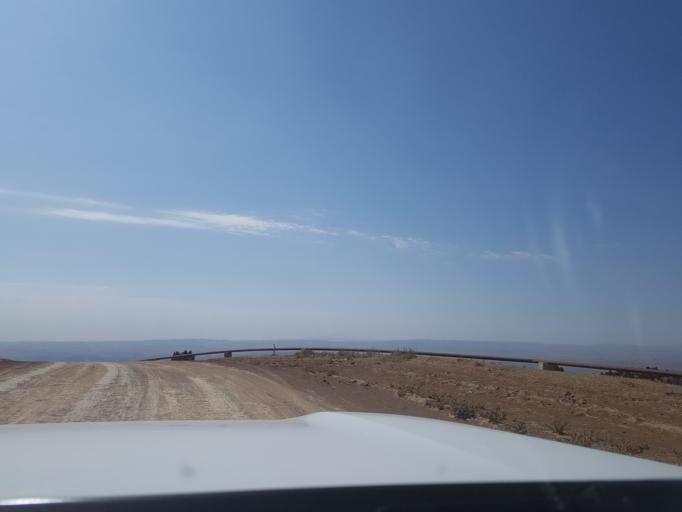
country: TM
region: Ahal
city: Baharly
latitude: 38.3216
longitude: 56.9530
